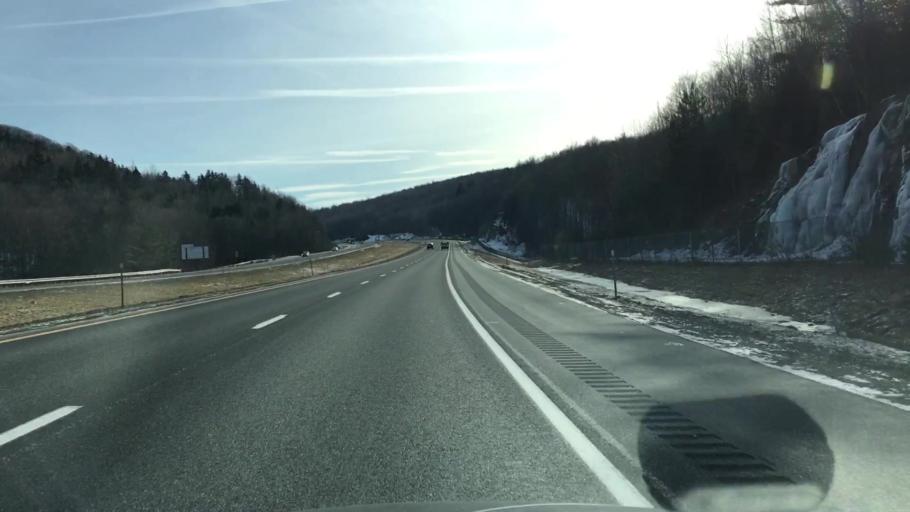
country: US
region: New Hampshire
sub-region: Grafton County
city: Enfield
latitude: 43.5801
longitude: -72.1617
